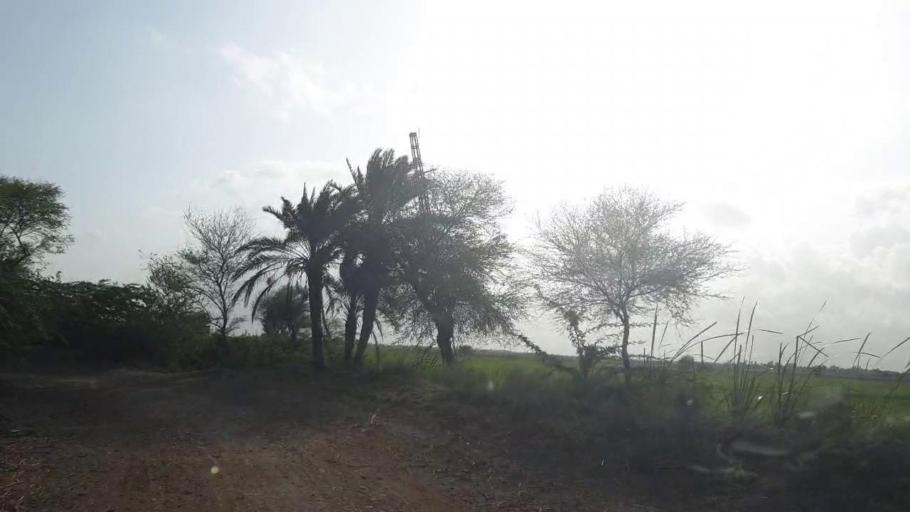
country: PK
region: Sindh
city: Kadhan
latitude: 24.6277
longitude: 69.0852
